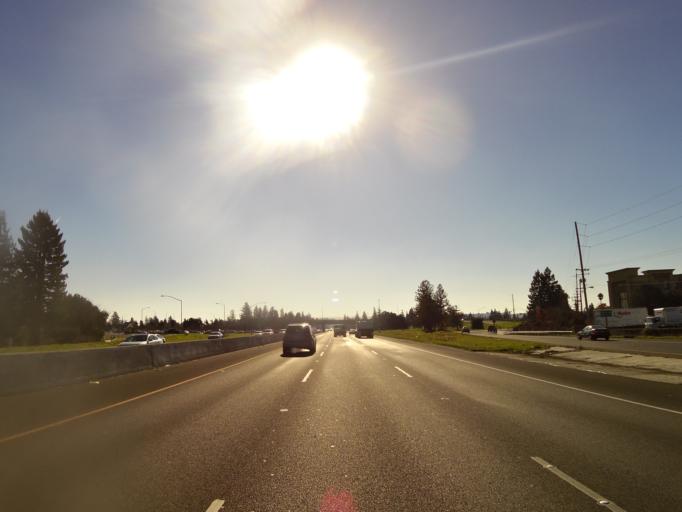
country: US
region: California
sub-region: Sonoma County
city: Rohnert Park
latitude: 38.3516
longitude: -122.7132
